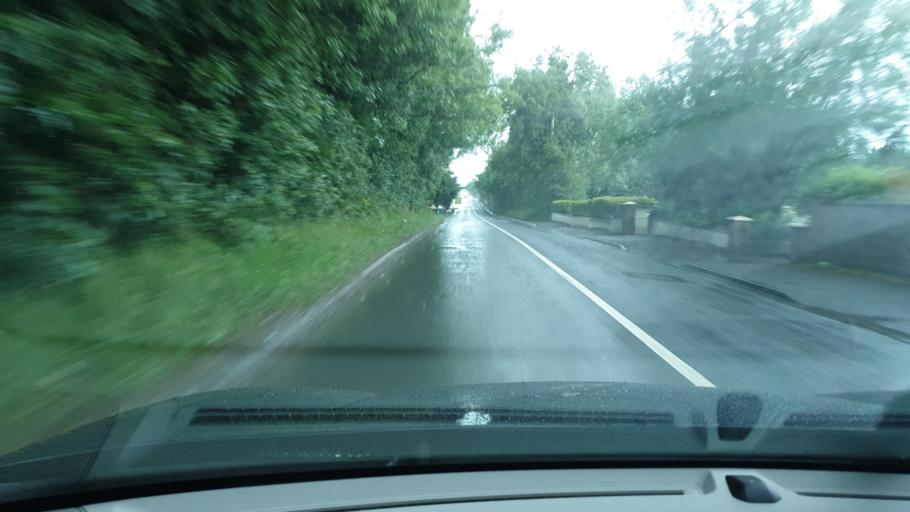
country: IE
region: Leinster
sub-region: An Mhi
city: Navan
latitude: 53.6324
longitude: -6.6883
